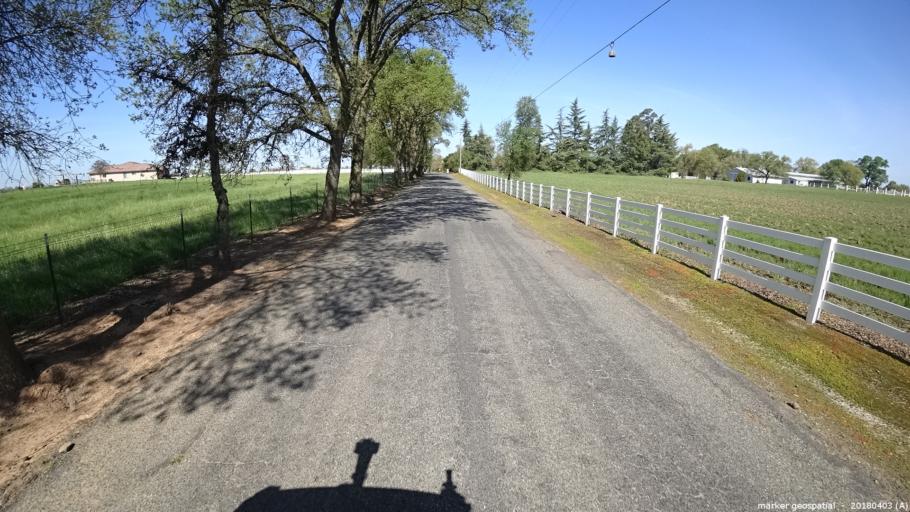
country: US
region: California
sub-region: Sacramento County
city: Wilton
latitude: 38.4362
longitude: -121.2255
